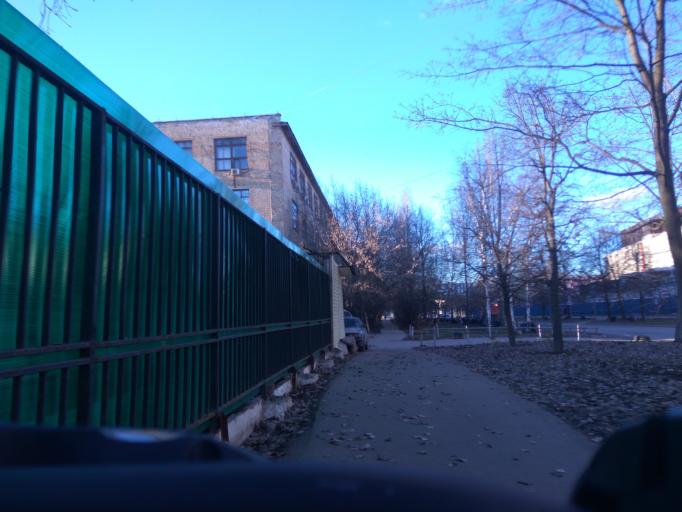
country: RU
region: Moscow
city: Ostankinskiy
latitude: 55.8193
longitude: 37.6031
